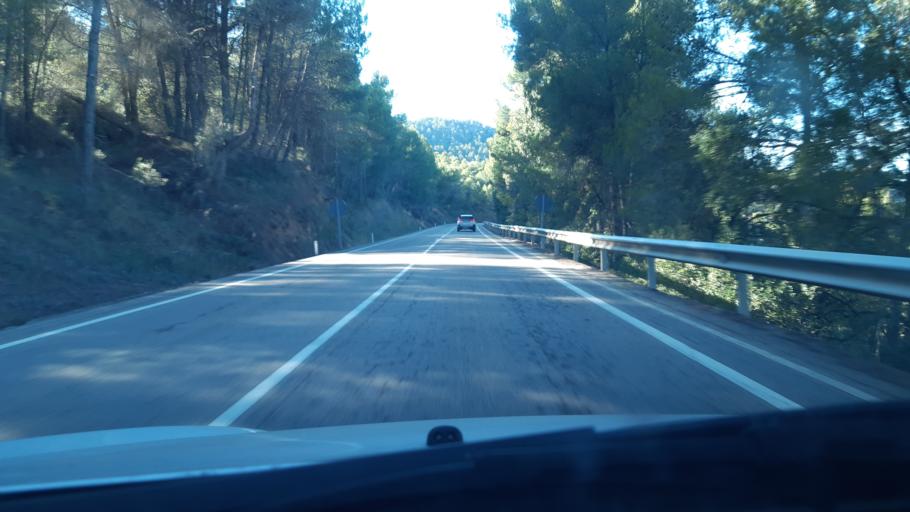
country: ES
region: Aragon
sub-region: Provincia de Teruel
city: Valderrobres
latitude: 40.8733
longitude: 0.1410
